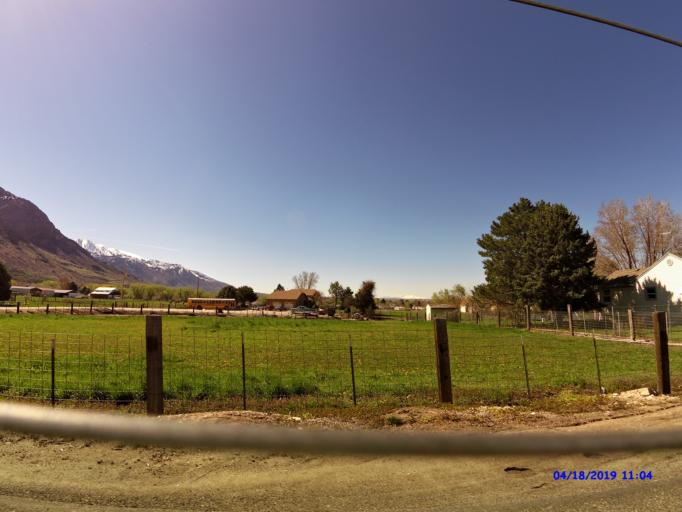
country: US
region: Utah
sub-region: Weber County
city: North Ogden
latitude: 41.2889
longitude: -111.9603
